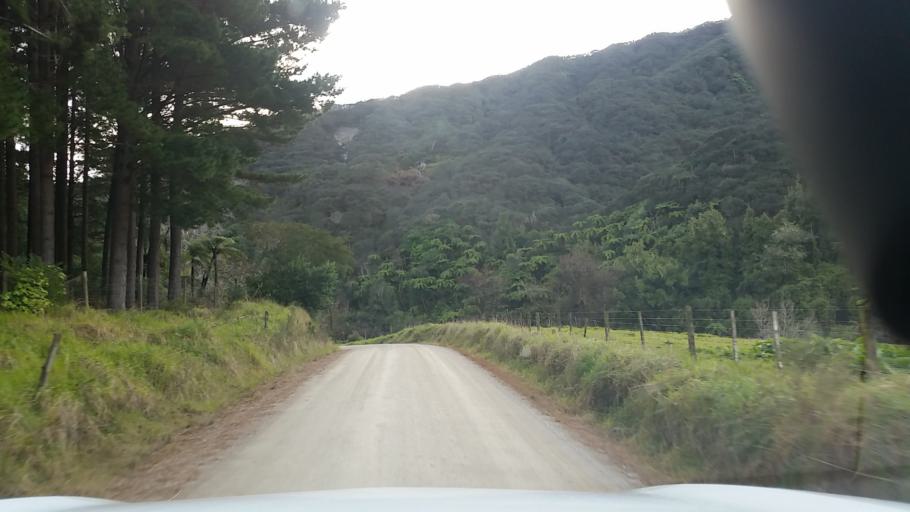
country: NZ
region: Taranaki
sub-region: South Taranaki District
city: Patea
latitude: -39.5723
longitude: 174.8219
